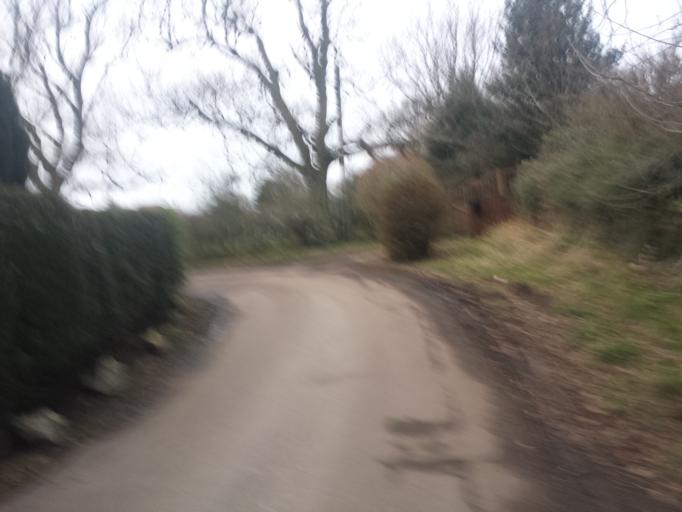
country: GB
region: England
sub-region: Essex
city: Little Clacton
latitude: 51.8409
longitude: 1.1314
